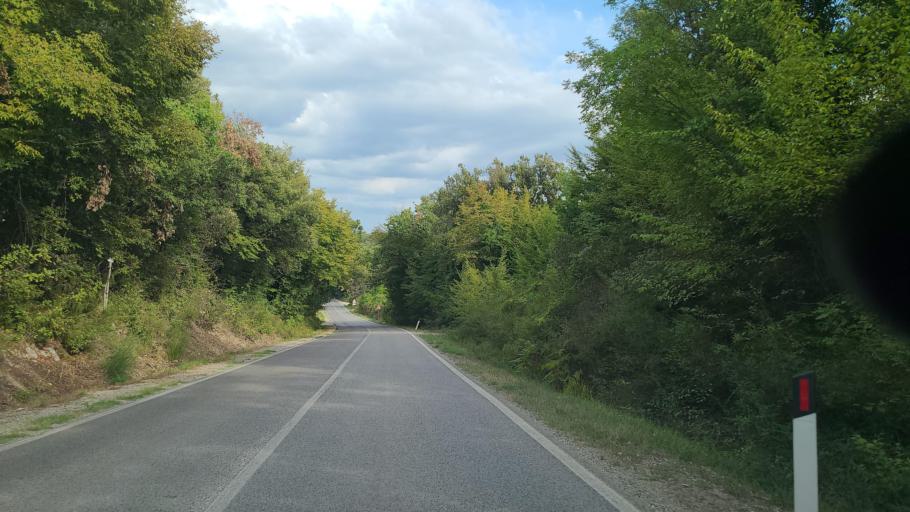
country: IT
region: Tuscany
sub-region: Provincia di Siena
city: San Gimignano
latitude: 43.4875
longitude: 10.9896
